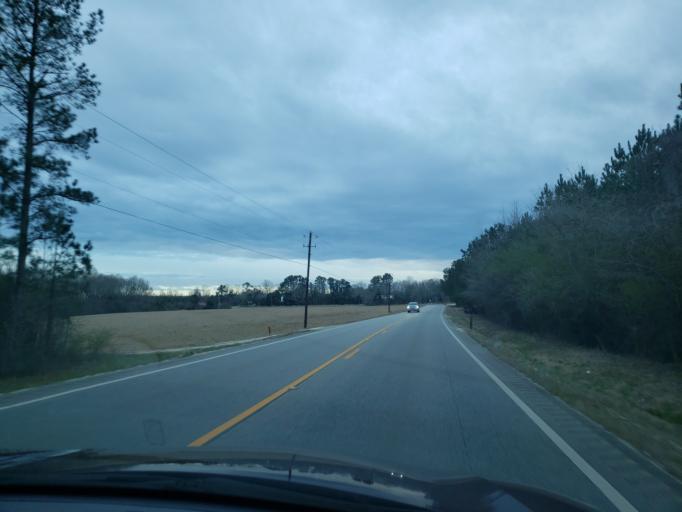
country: US
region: Alabama
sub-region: Chambers County
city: Lafayette
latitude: 32.9842
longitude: -85.4028
